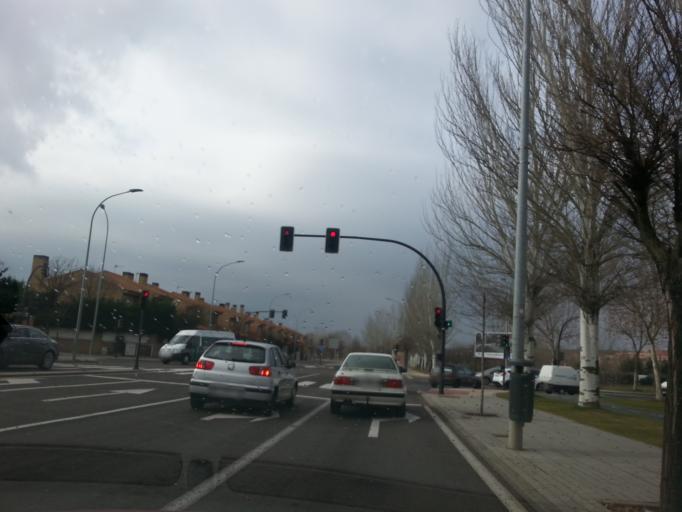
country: ES
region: Castille and Leon
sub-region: Provincia de Salamanca
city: Salamanca
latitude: 40.9581
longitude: -5.6812
